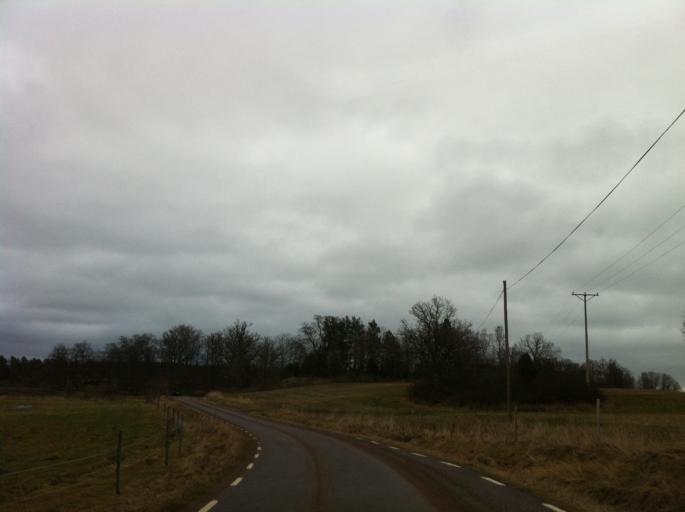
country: SE
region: Kalmar
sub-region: Vasterviks Kommun
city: Vaestervik
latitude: 57.9155
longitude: 16.6289
